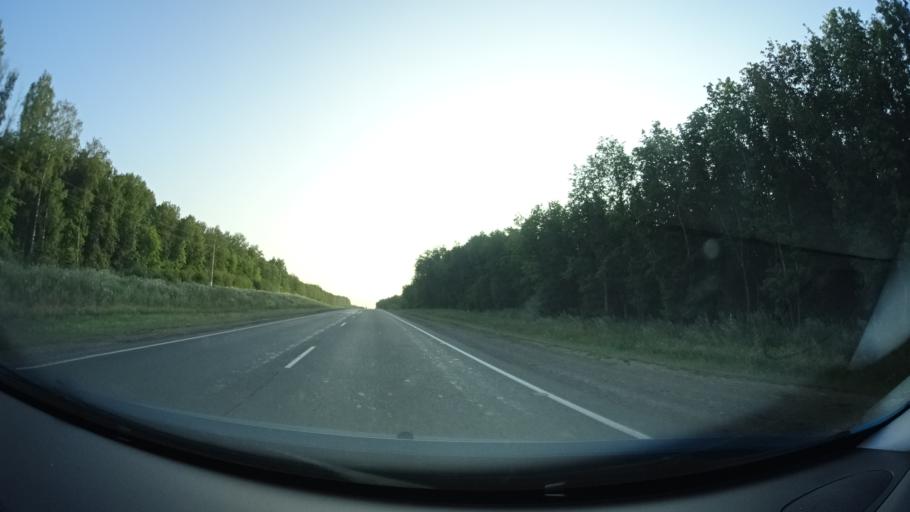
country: RU
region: Samara
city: Isakly
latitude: 54.0100
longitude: 51.6685
